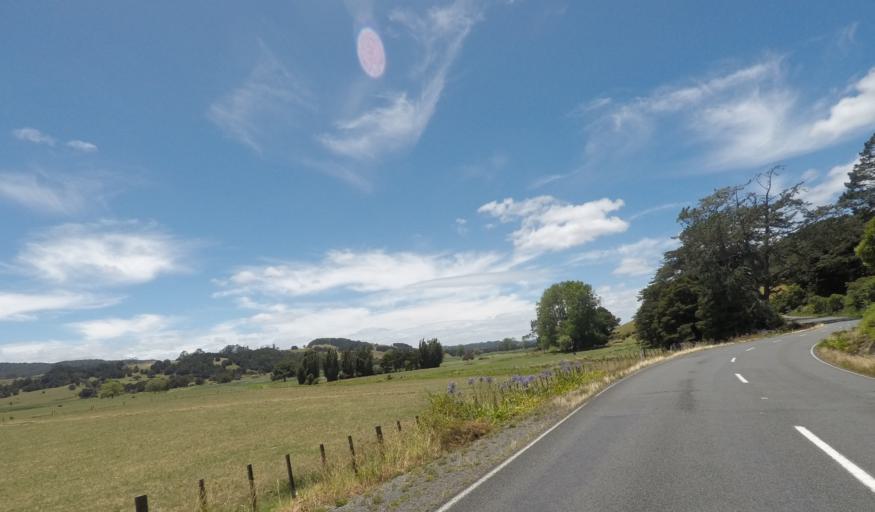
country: NZ
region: Northland
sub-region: Whangarei
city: Whangarei
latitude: -35.5368
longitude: 174.3111
